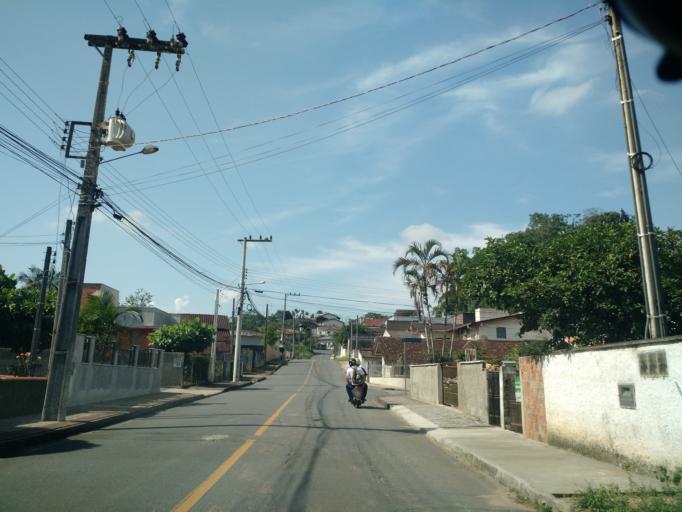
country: BR
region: Santa Catarina
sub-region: Jaragua Do Sul
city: Jaragua do Sul
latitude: -26.4951
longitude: -49.1018
